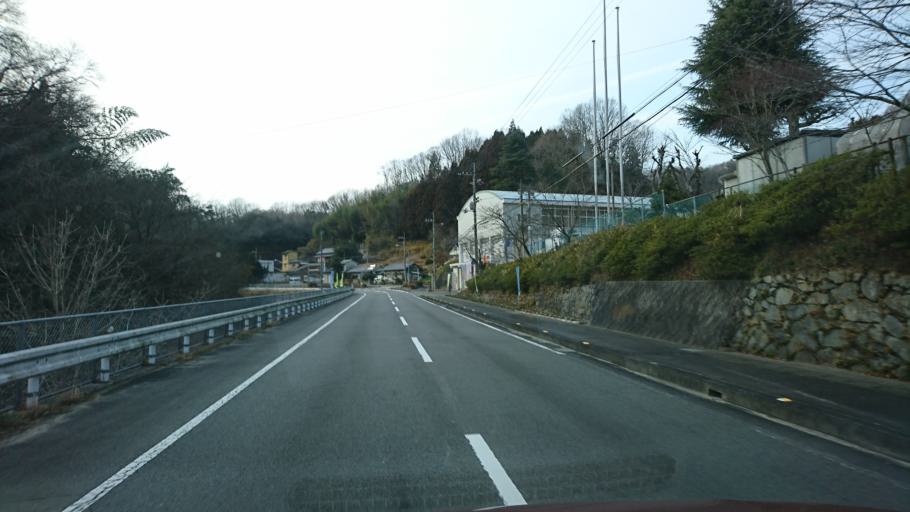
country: JP
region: Ehime
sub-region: Shikoku-chuo Shi
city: Matsuyama
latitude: 33.9027
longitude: 132.8191
